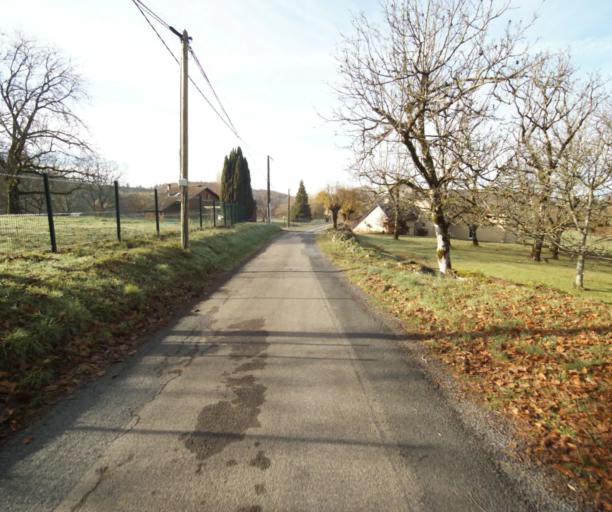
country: FR
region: Limousin
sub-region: Departement de la Correze
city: Sainte-Fortunade
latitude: 45.2233
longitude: 1.7437
